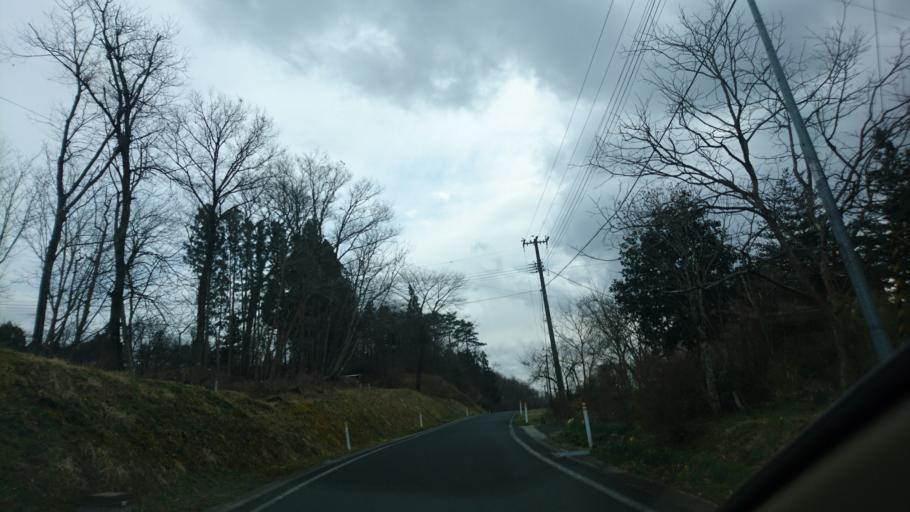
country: JP
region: Iwate
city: Ichinoseki
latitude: 38.8978
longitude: 141.1715
